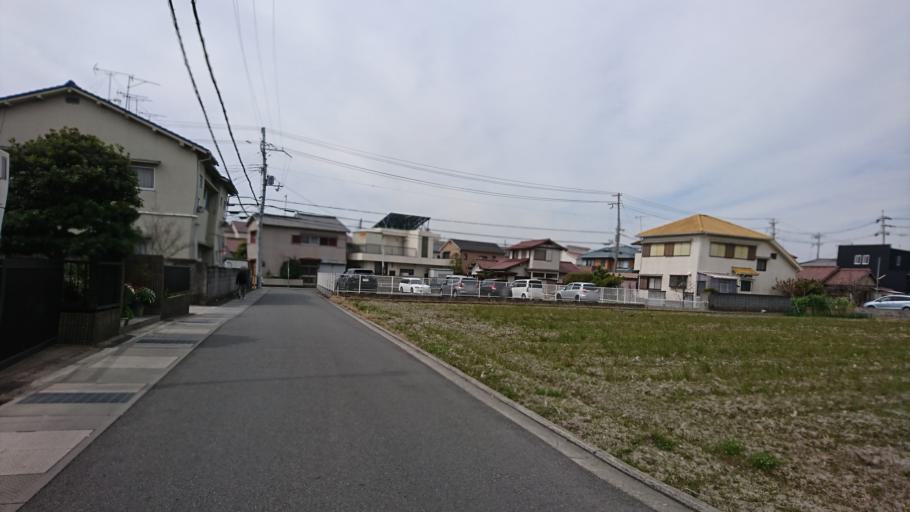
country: JP
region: Hyogo
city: Kakogawacho-honmachi
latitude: 34.7308
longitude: 134.8845
